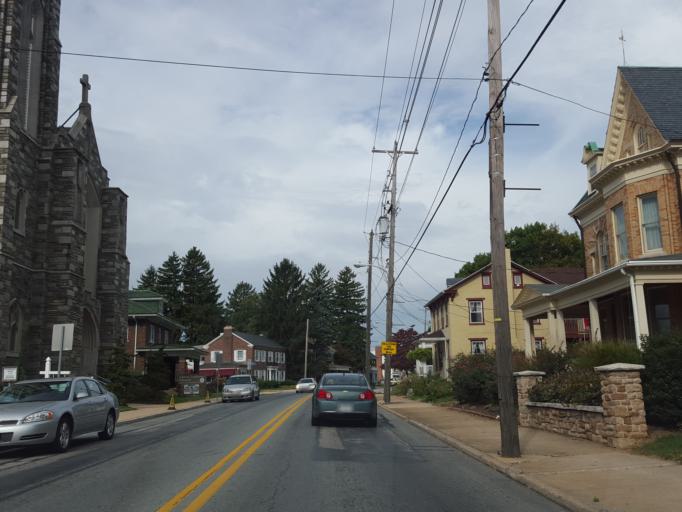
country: US
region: Pennsylvania
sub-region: York County
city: Dallastown
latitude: 39.9015
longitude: -76.6469
